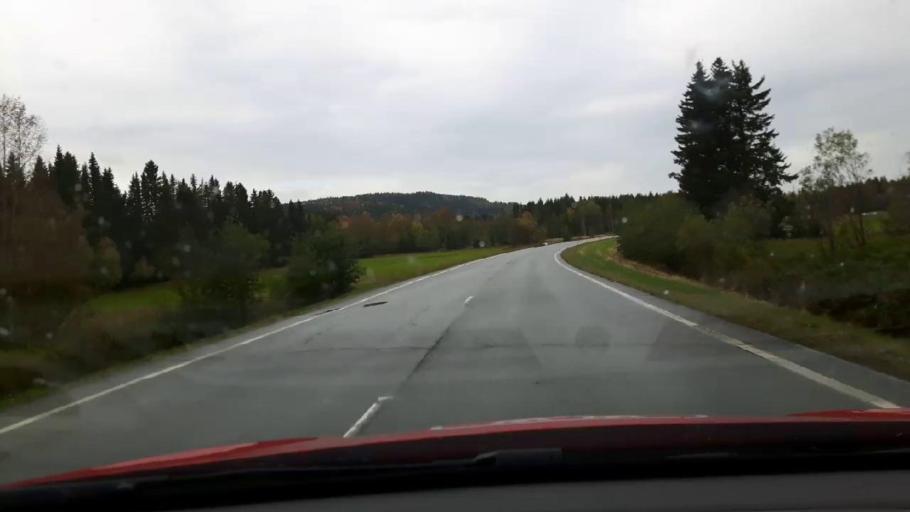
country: SE
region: Jaemtland
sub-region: Bergs Kommun
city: Hoverberg
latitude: 62.9050
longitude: 14.3363
